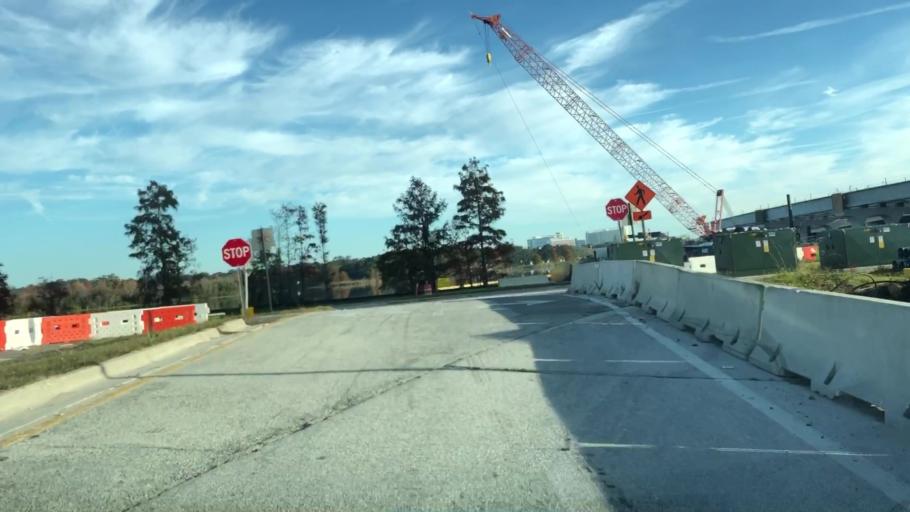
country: US
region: Florida
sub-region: Orange County
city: Orlando
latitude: 28.5596
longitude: -81.3816
